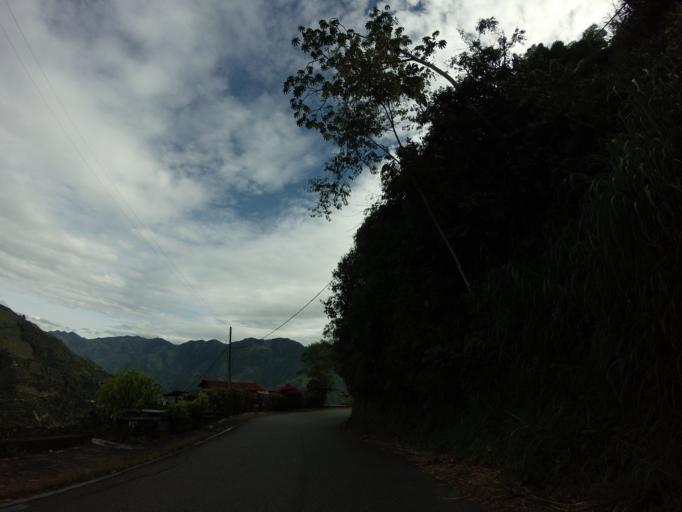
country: CO
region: Tolima
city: Casabianca
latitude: 5.1436
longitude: -75.1303
